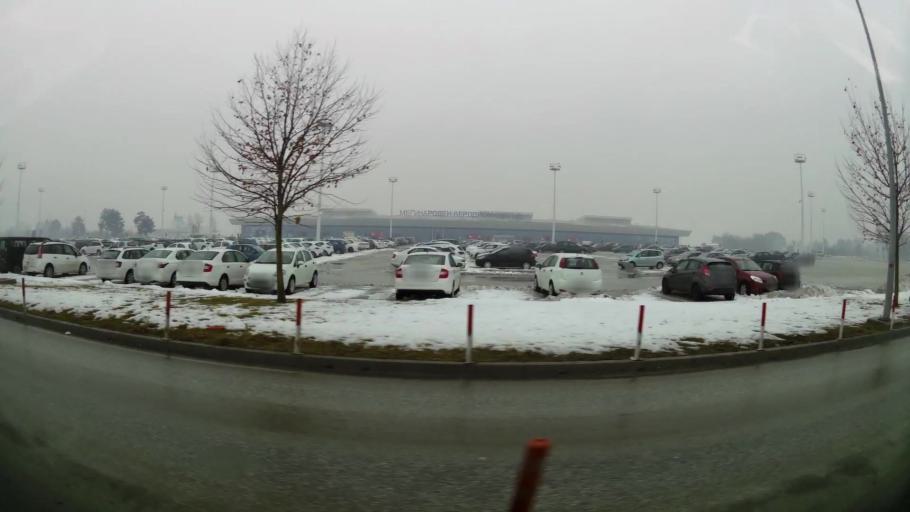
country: MK
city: Miladinovci
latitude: 41.9614
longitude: 21.6298
